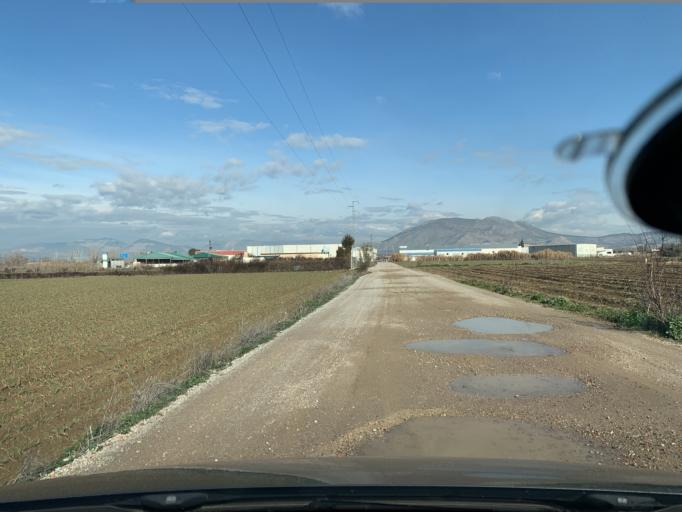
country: ES
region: Andalusia
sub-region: Provincia de Granada
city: Chauchina
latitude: 37.1859
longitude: -3.7493
